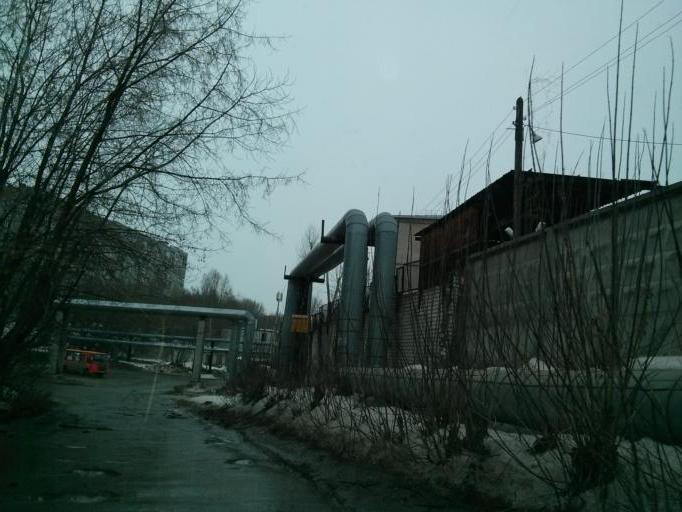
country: RU
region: Nizjnij Novgorod
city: Nizhniy Novgorod
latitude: 56.3161
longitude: 44.0434
